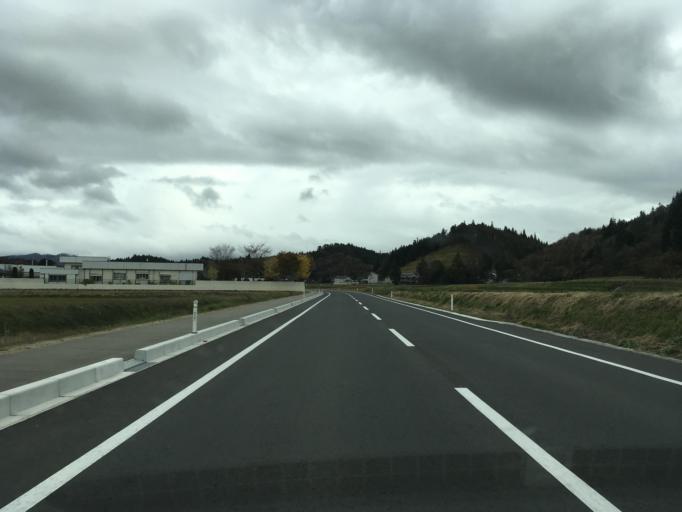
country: JP
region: Iwate
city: Ichinoseki
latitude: 39.0164
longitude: 141.3432
